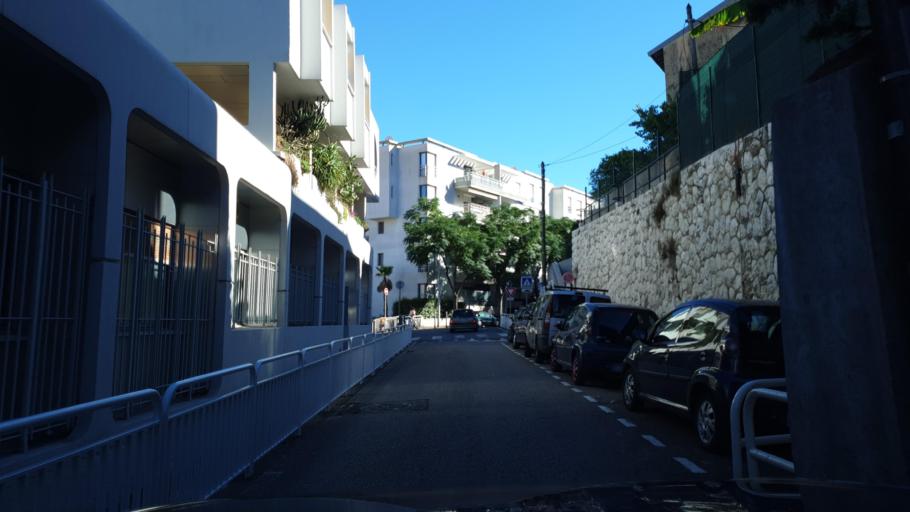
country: FR
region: Provence-Alpes-Cote d'Azur
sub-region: Departement des Alpes-Maritimes
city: Nice
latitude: 43.7092
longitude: 7.2795
